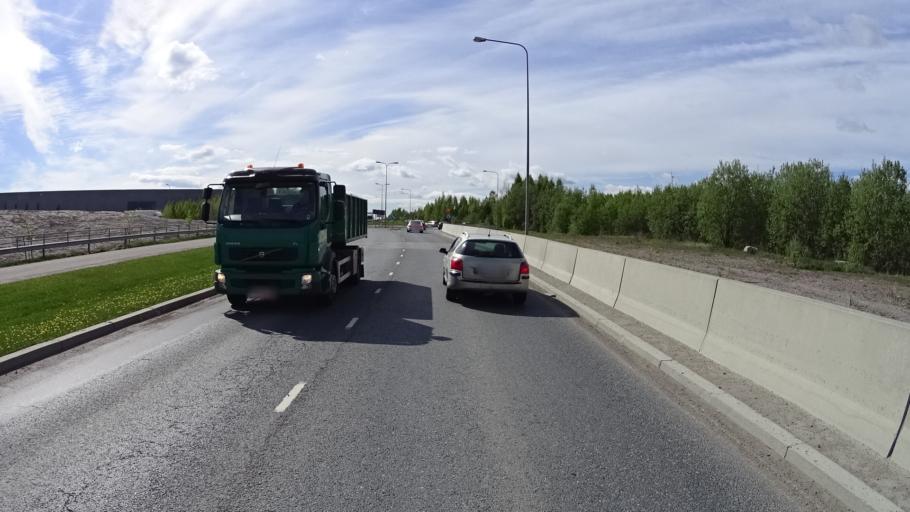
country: FI
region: Uusimaa
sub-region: Helsinki
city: Vantaa
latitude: 60.3036
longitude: 24.9190
